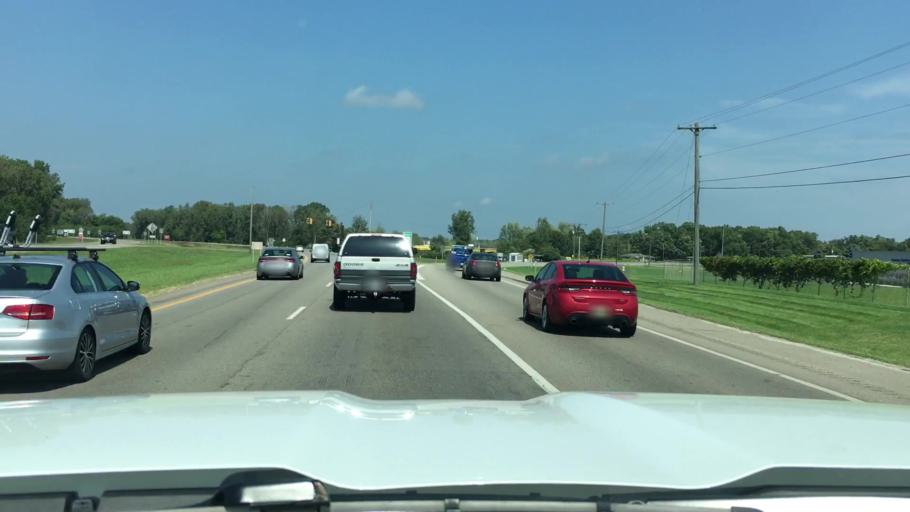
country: US
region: Michigan
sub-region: Kalamazoo County
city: Schoolcraft
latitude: 42.1443
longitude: -85.6376
